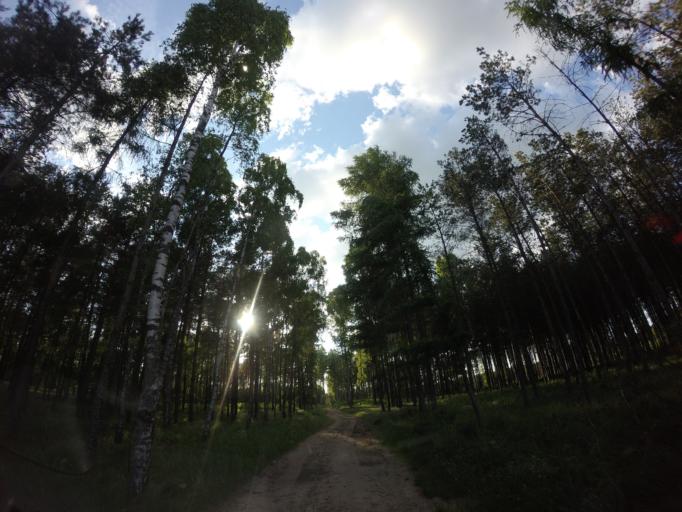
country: PL
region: West Pomeranian Voivodeship
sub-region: Powiat choszczenski
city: Drawno
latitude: 53.1928
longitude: 15.8661
